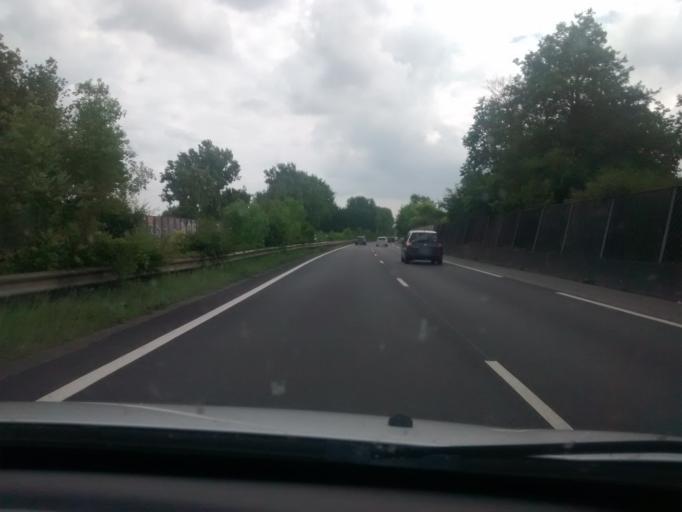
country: FR
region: Ile-de-France
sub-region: Departement des Yvelines
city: Le Perray-en-Yvelines
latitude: 48.6910
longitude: 1.8441
